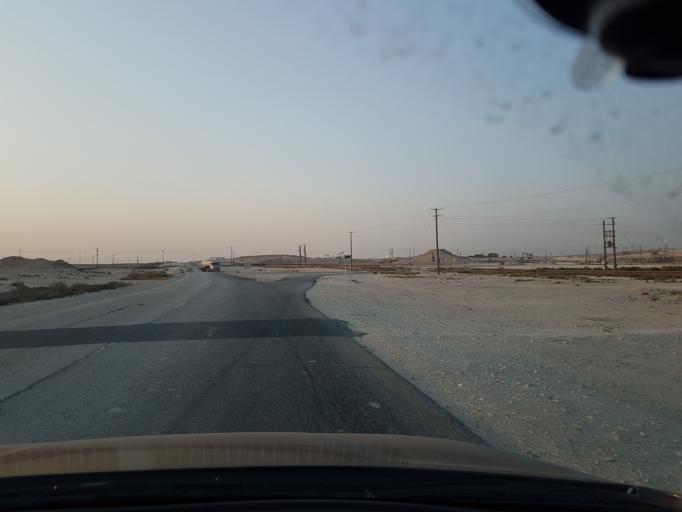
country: BH
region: Central Governorate
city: Dar Kulayb
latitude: 26.0521
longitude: 50.5568
